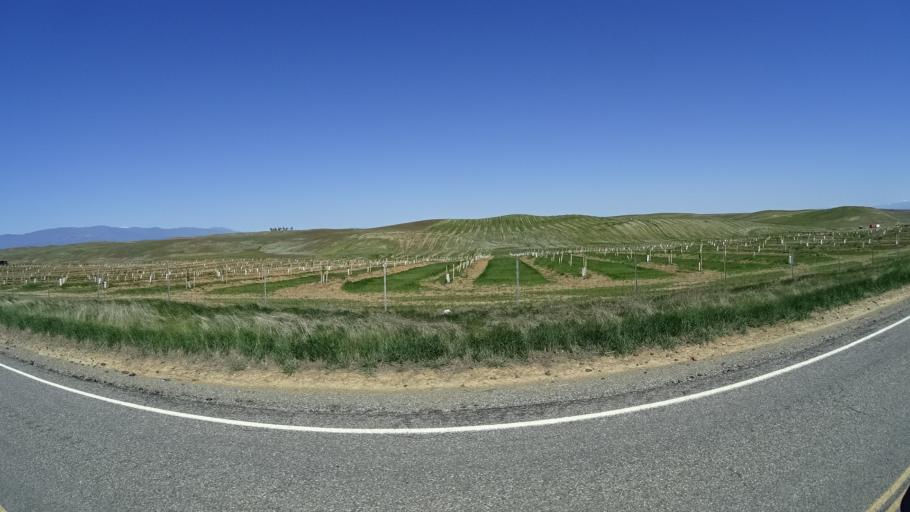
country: US
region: California
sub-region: Glenn County
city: Orland
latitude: 39.8312
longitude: -122.3456
